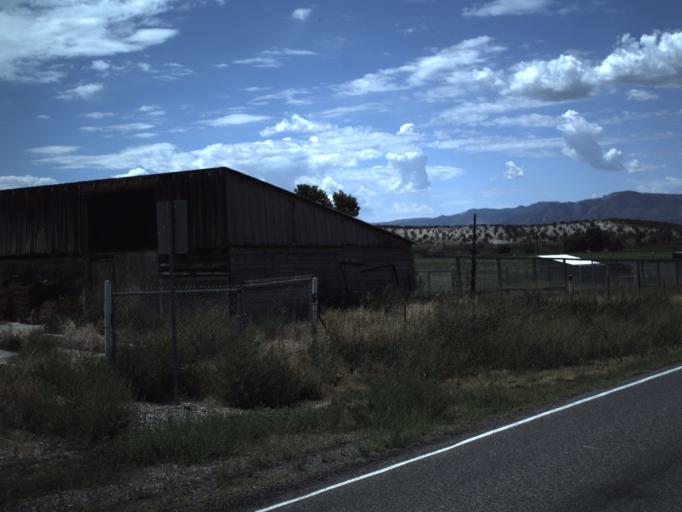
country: US
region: Utah
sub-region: Sanpete County
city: Mount Pleasant
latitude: 39.4818
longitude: -111.5010
